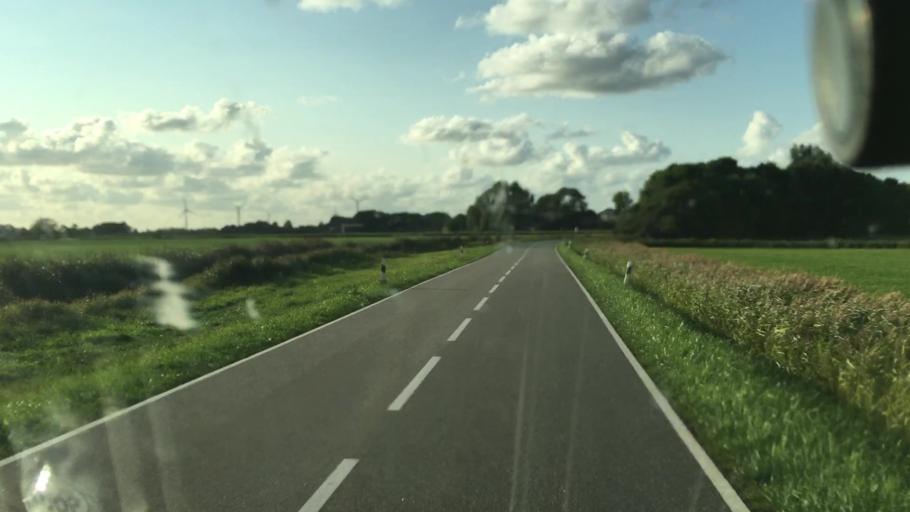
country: DE
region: Lower Saxony
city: Wittmund
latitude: 53.6346
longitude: 7.8308
